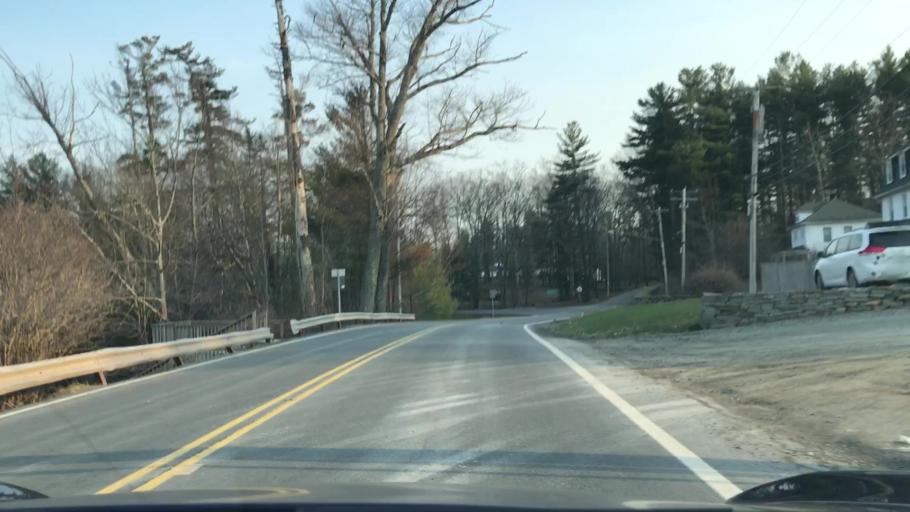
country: US
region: New York
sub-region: Sullivan County
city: Liberty
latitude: 41.6800
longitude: -74.9930
